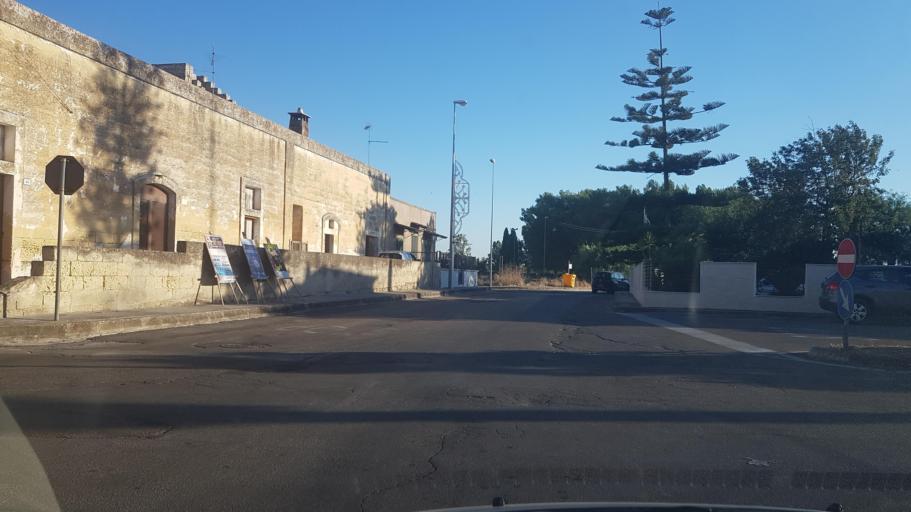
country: IT
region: Apulia
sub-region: Provincia di Lecce
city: Struda
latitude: 40.3188
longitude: 18.2824
